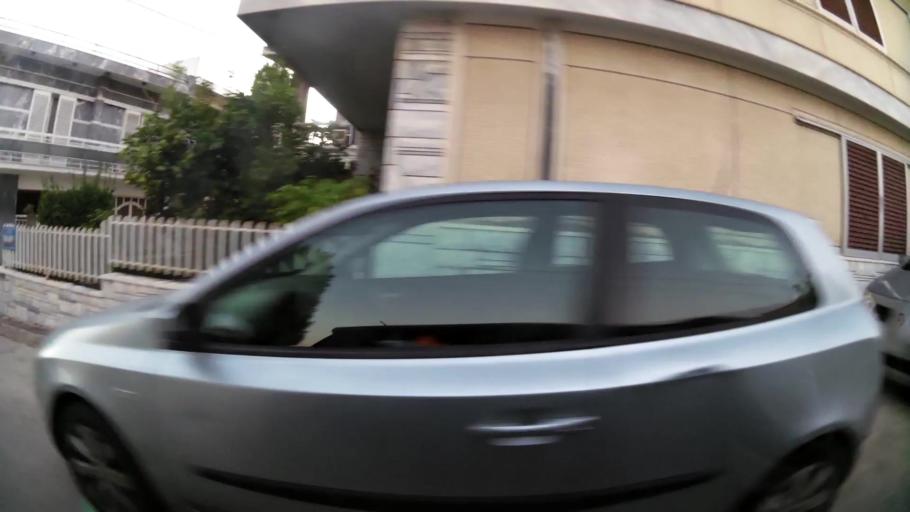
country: GR
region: Attica
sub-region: Nomarchia Anatolikis Attikis
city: Spata
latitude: 37.9629
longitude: 23.9109
